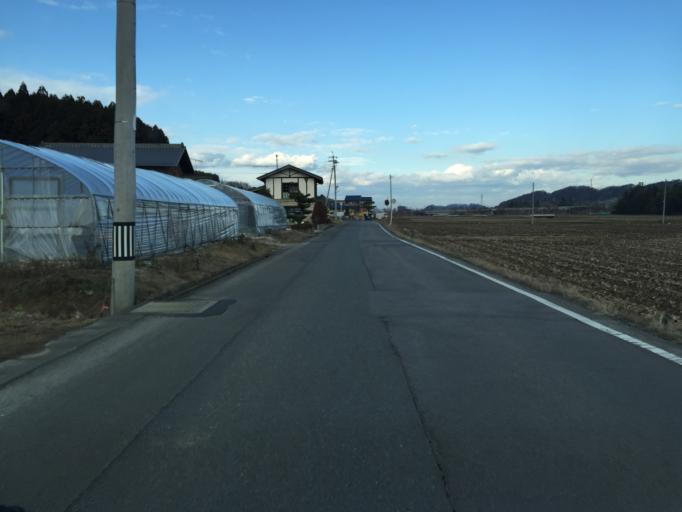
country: JP
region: Fukushima
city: Fukushima-shi
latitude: 37.7027
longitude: 140.4448
